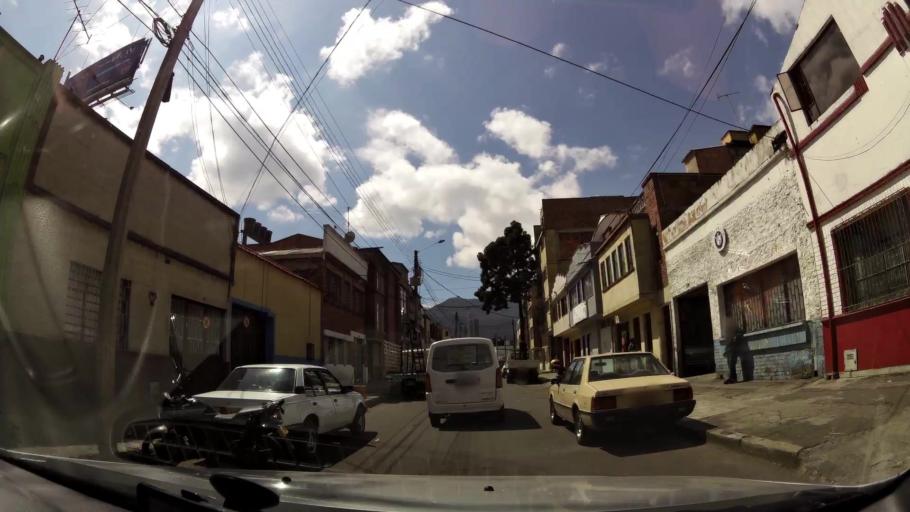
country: CO
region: Bogota D.C.
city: Bogota
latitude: 4.6221
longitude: -74.0785
